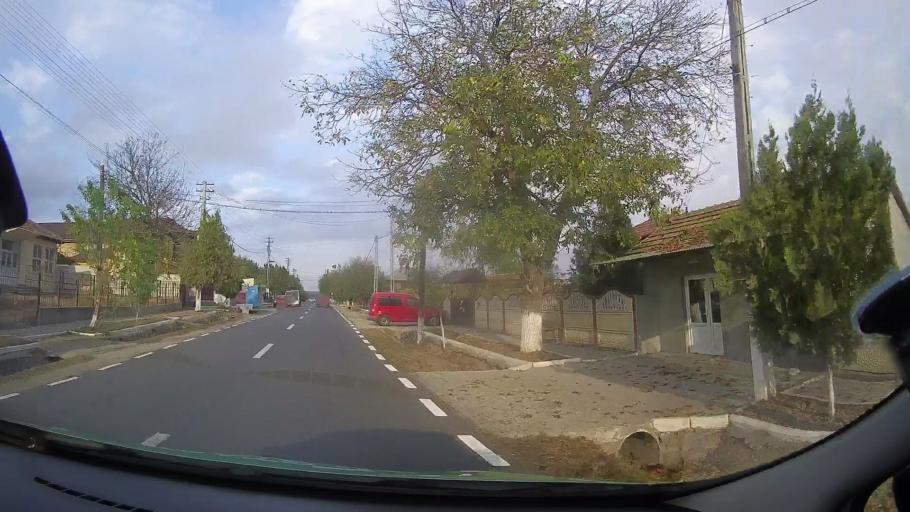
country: RO
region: Constanta
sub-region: Comuna Mircea Voda
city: Mircea Voda
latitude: 44.2795
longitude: 28.1748
